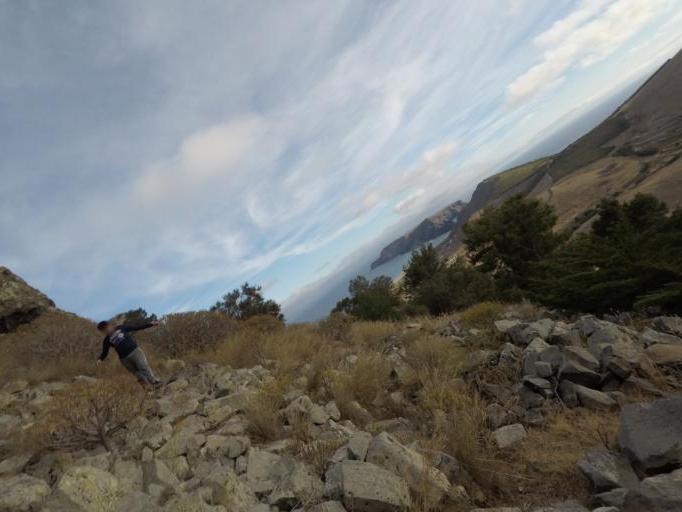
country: PT
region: Madeira
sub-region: Porto Santo
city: Vila de Porto Santo
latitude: 33.0434
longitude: -16.3710
